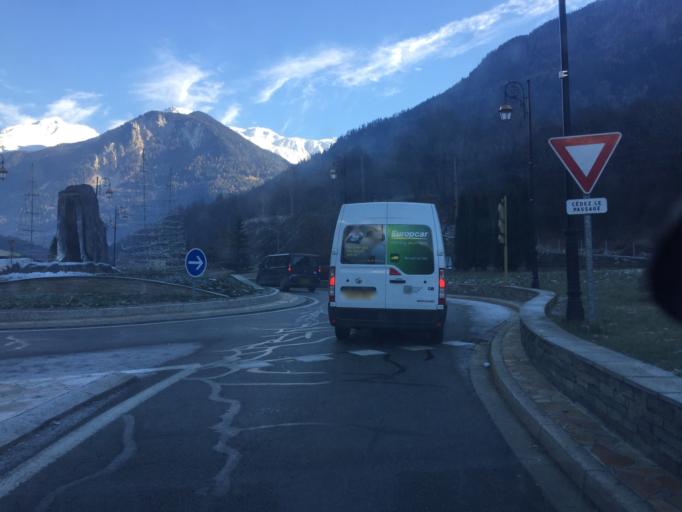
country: FR
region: Rhone-Alpes
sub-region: Departement de la Savoie
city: Modane
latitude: 45.1945
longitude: 6.6290
